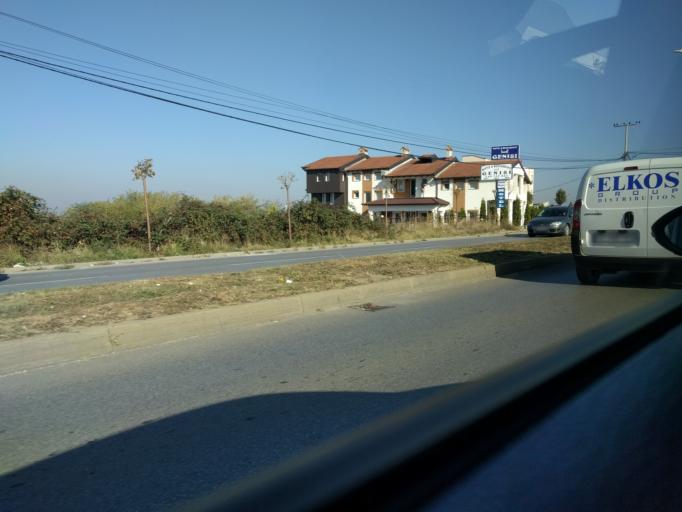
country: XK
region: Prizren
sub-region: Prizren
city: Prizren
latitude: 42.2321
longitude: 20.7571
